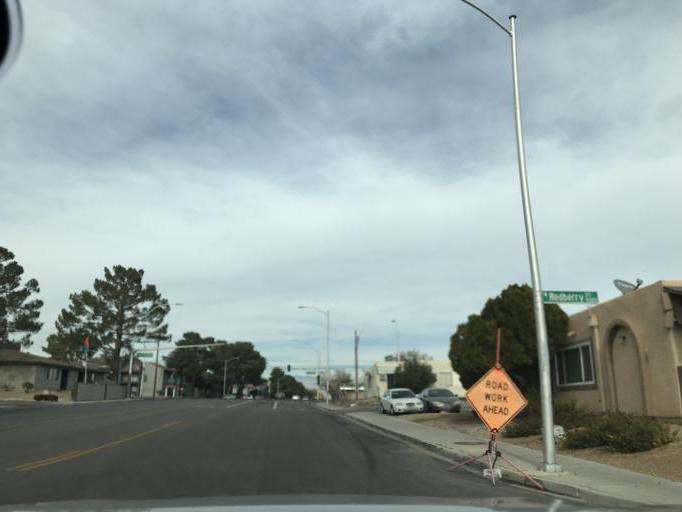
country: US
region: Nevada
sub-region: Clark County
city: Las Vegas
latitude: 36.2161
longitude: -115.2166
